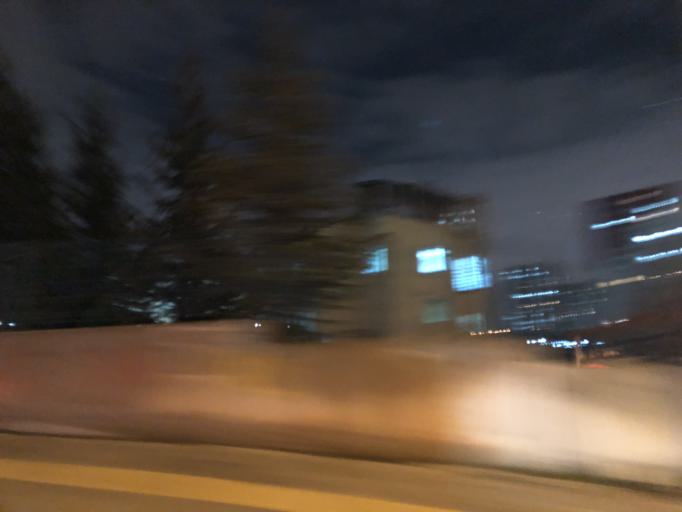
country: TR
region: Ankara
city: Batikent
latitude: 39.9665
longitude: 32.7758
